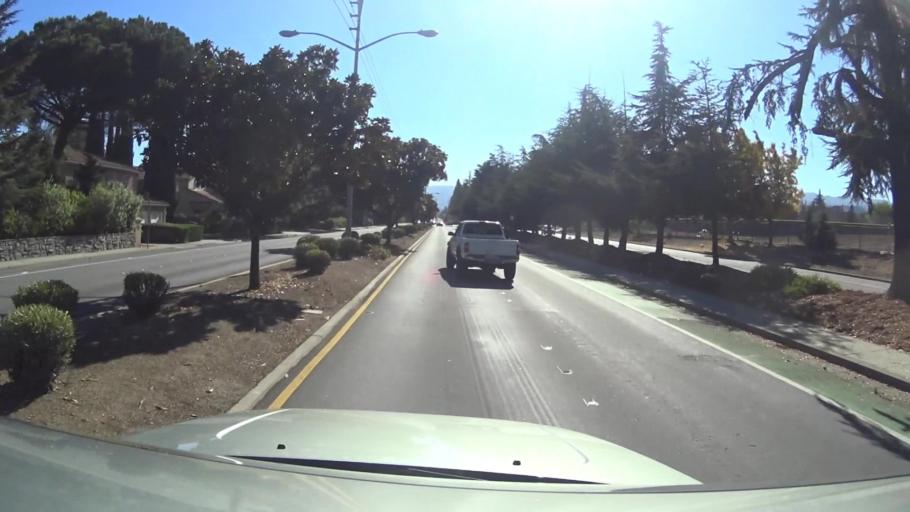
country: US
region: California
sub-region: Santa Clara County
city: Cupertino
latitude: 37.3177
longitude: -122.0416
